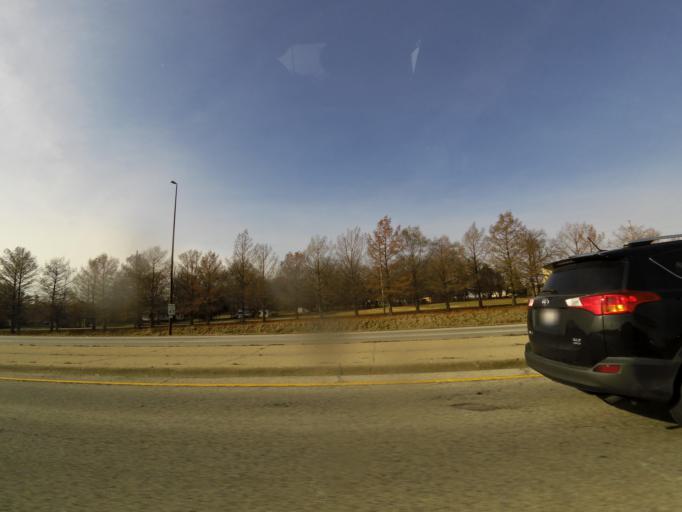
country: US
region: Illinois
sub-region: Macon County
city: Forsyth
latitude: 39.9142
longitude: -88.9553
